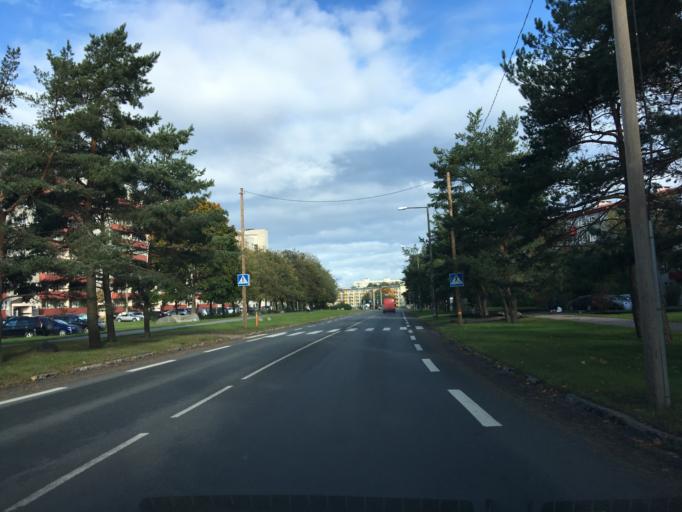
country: EE
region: Harju
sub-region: Tallinna linn
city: Tallinn
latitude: 59.3964
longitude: 24.6824
